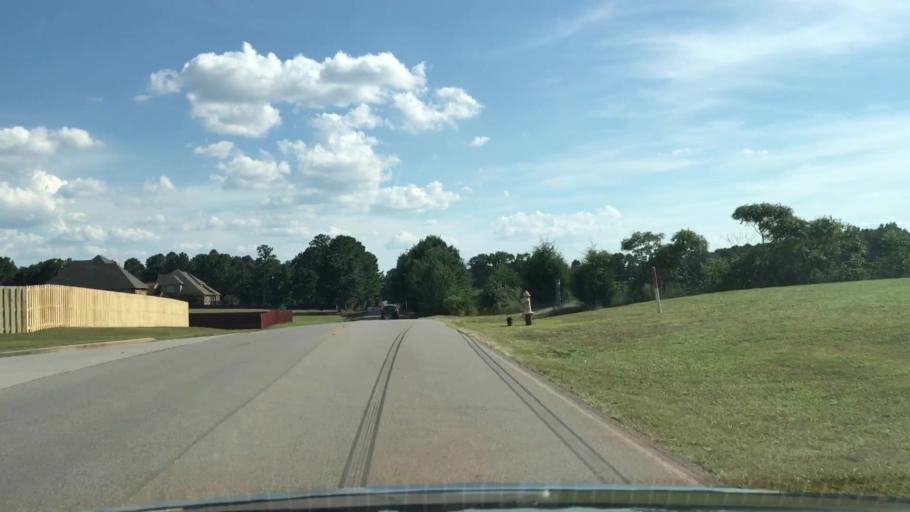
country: US
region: Alabama
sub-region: Madison County
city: Harvest
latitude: 34.8922
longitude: -86.7487
